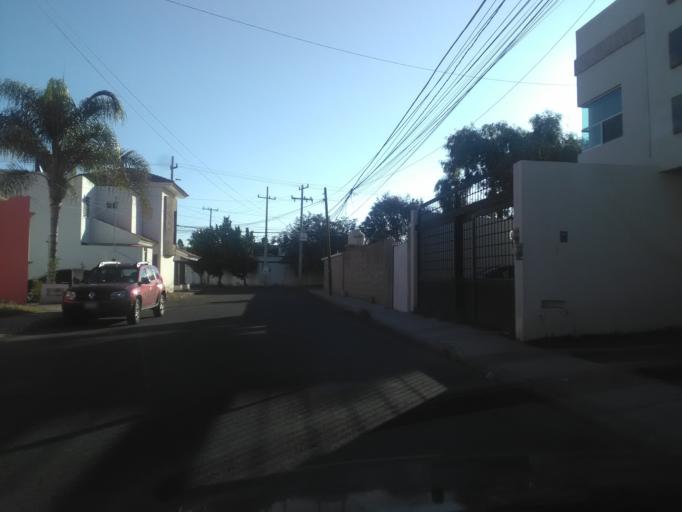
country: MX
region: Durango
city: Victoria de Durango
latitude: 24.0005
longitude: -104.7030
